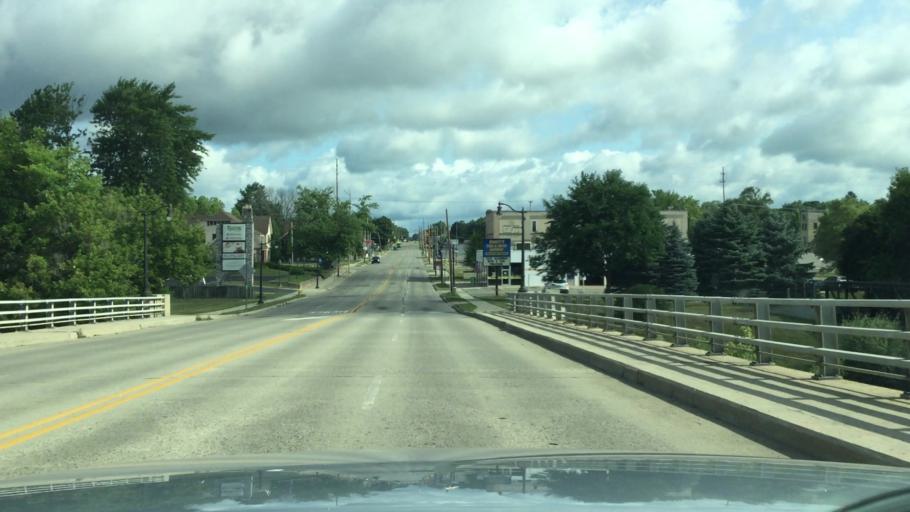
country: US
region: Michigan
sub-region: Montcalm County
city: Greenville
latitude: 43.1829
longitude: -85.2531
